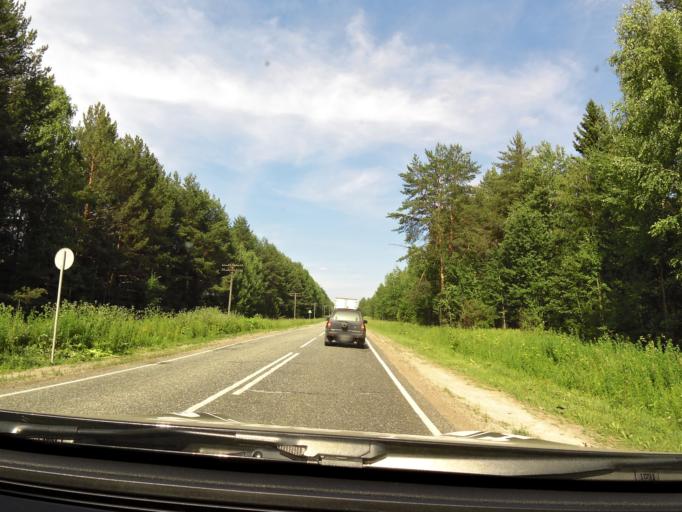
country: RU
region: Kirov
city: Slobodskoy
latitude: 58.7898
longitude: 50.5141
